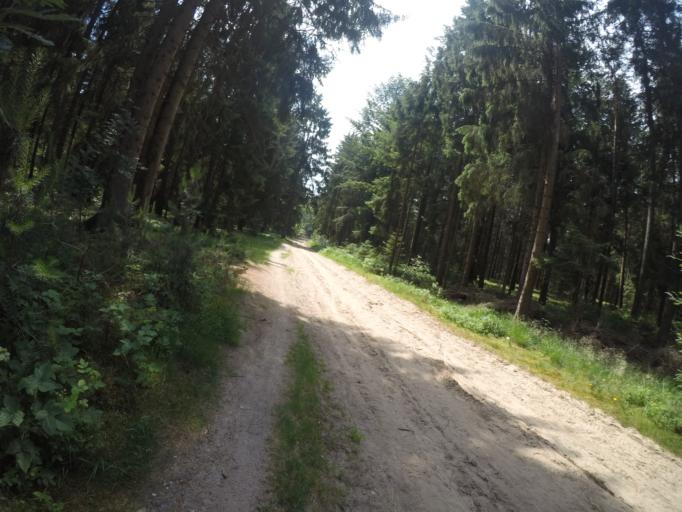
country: DE
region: Lower Saxony
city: Handeloh
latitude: 53.2892
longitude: 9.8446
